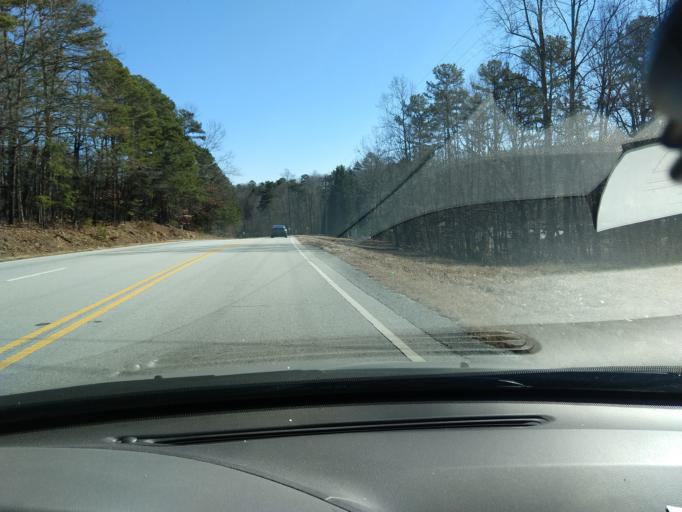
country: US
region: Georgia
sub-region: Stephens County
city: Toccoa
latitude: 34.6094
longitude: -83.3710
